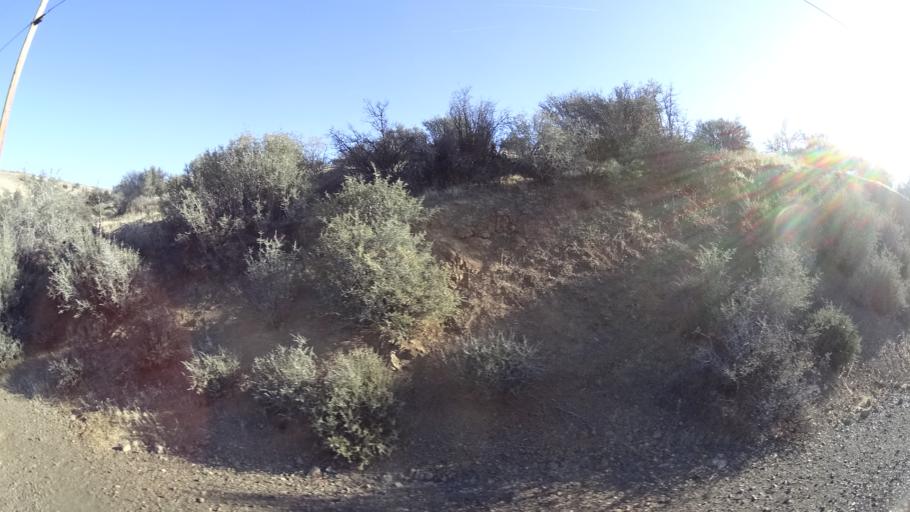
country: US
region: California
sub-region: Siskiyou County
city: Montague
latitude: 41.8967
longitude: -122.4891
